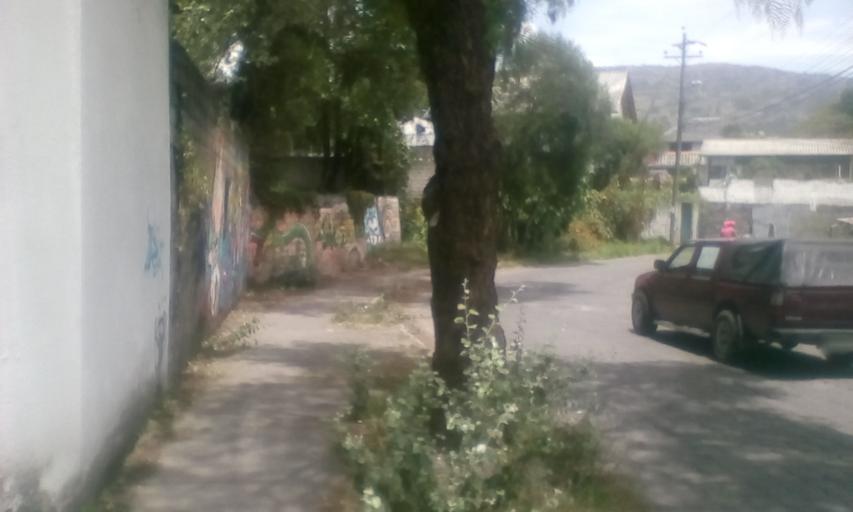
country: EC
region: Pichincha
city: Sangolqui
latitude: -0.2984
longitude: -78.4817
